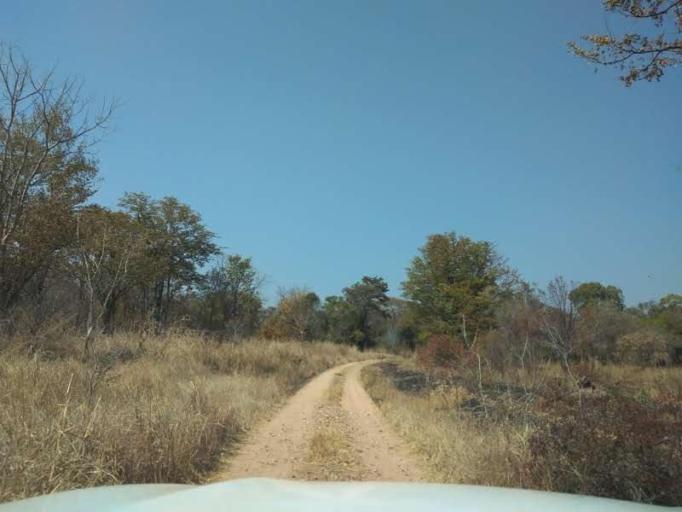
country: ZM
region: Eastern
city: Nyimba
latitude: -14.1516
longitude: 30.1402
